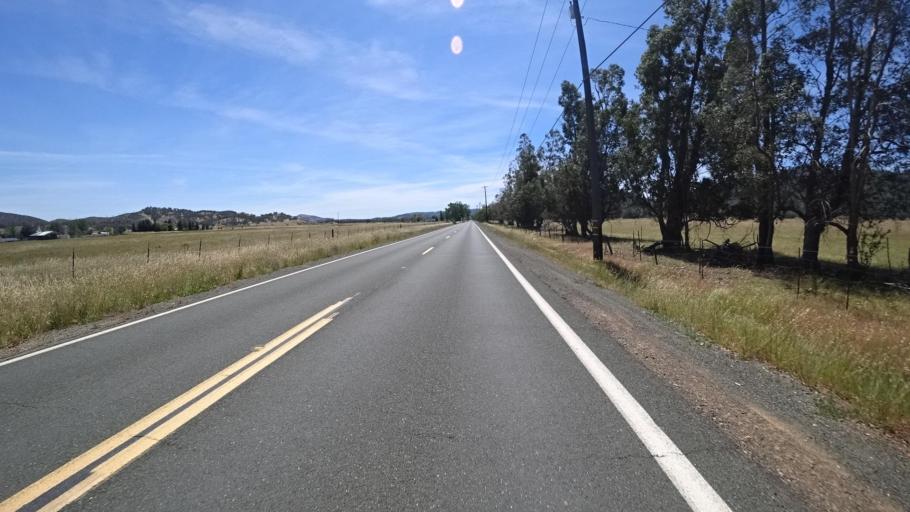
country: US
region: California
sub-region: Lake County
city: Middletown
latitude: 38.7449
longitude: -122.5764
